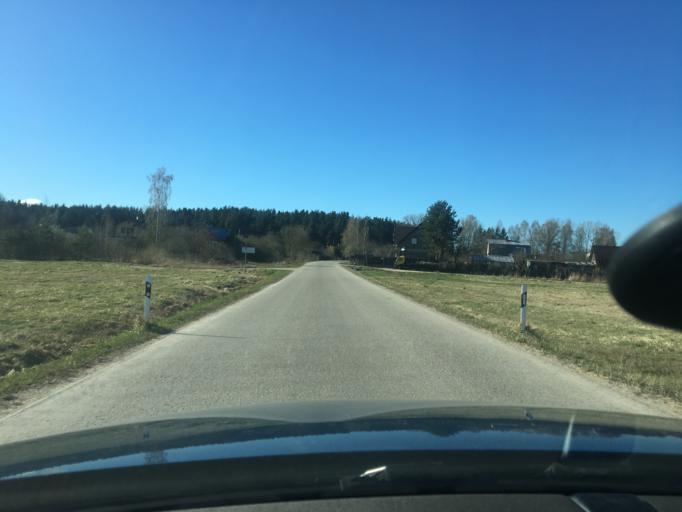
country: LV
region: Kekava
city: Kekava
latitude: 56.8528
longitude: 24.2585
